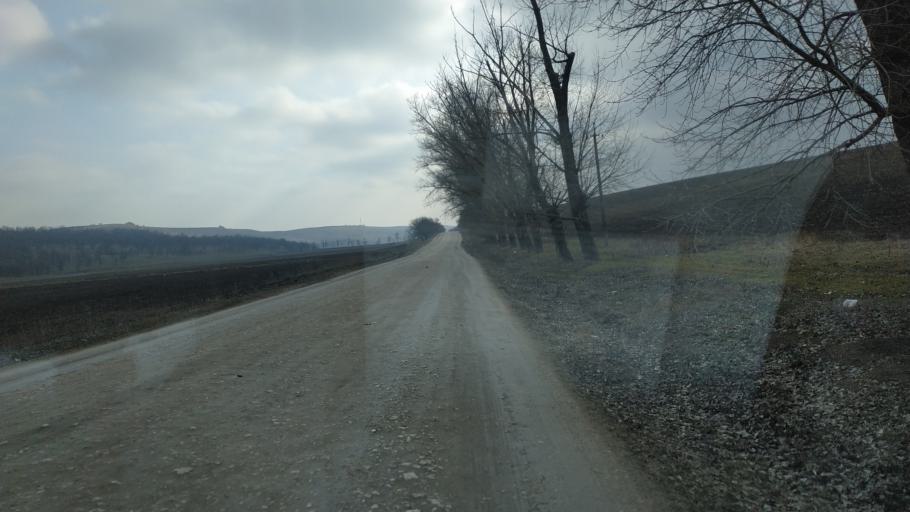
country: MD
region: Hincesti
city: Dancu
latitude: 46.9280
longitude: 28.3278
